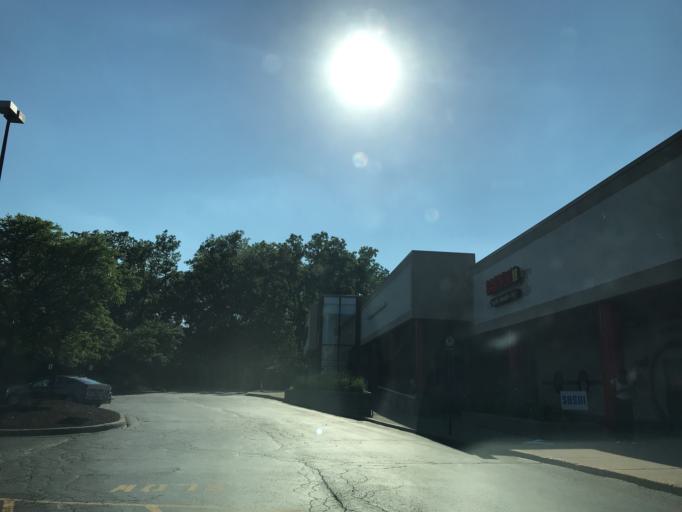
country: US
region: Michigan
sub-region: Oakland County
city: Farmington Hills
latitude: 42.4992
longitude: -83.4205
